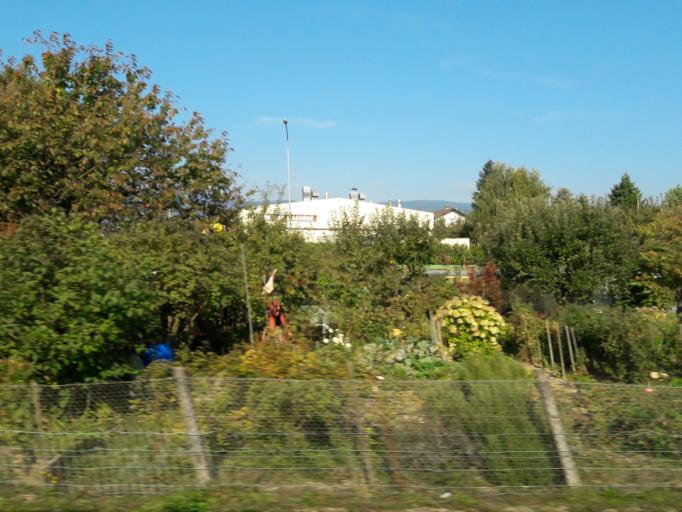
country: CH
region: Vaud
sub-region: Nyon District
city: Prangins
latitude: 46.3956
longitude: 6.2444
